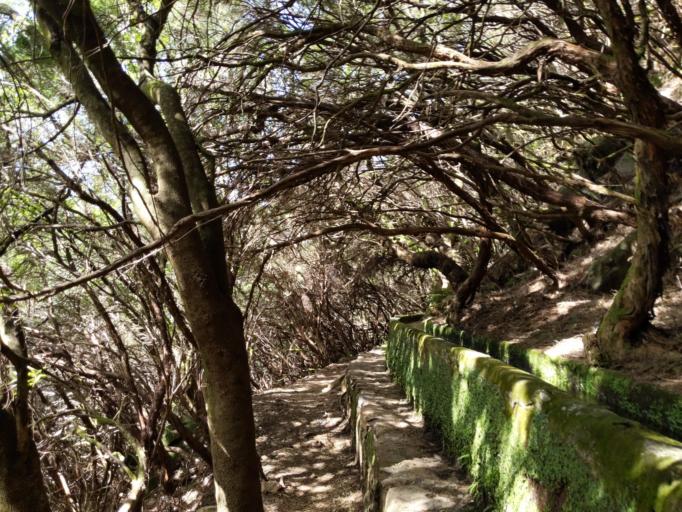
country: PT
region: Madeira
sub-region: Calheta
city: Arco da Calheta
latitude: 32.7659
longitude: -17.1294
